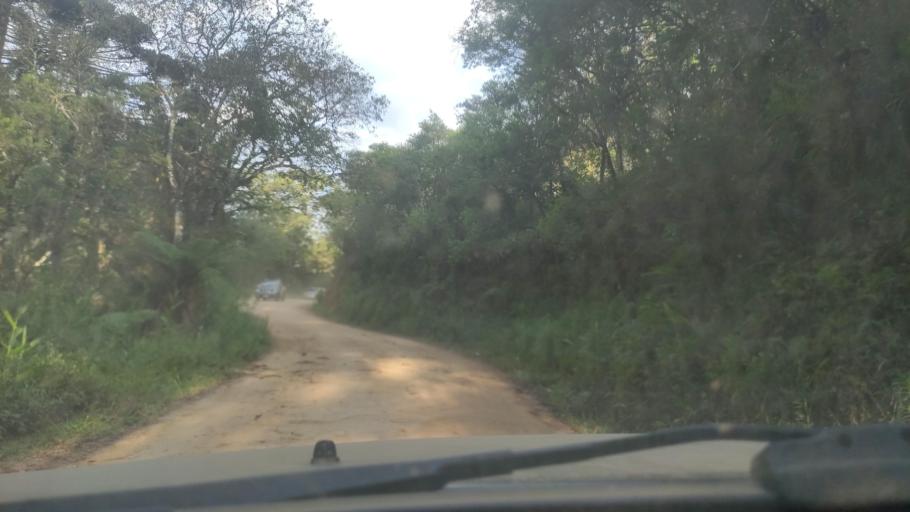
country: BR
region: Minas Gerais
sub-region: Cambui
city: Cambui
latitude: -22.7492
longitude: -45.9261
